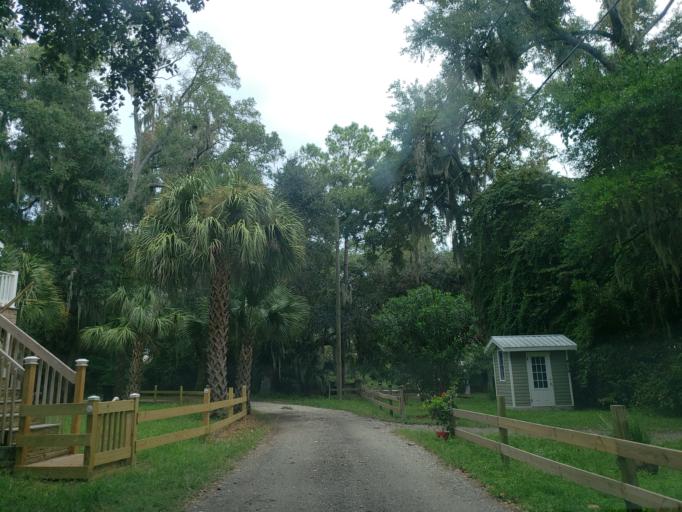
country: US
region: Georgia
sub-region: Chatham County
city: Wilmington Island
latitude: 31.9775
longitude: -80.9950
